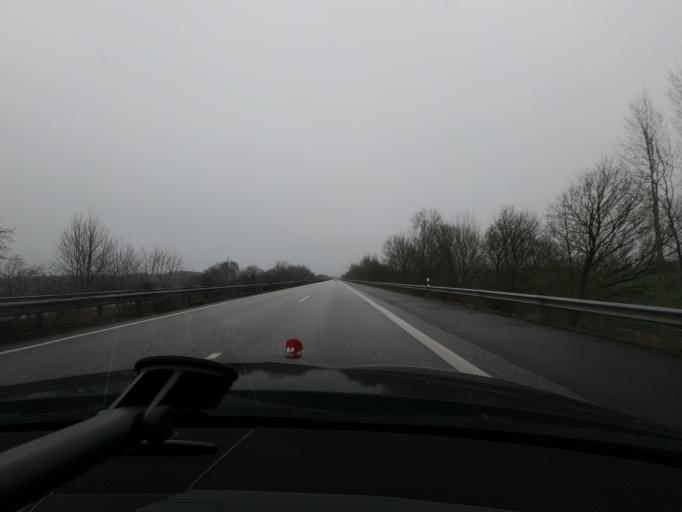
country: DE
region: Schleswig-Holstein
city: Bollingstedt
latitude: 54.6002
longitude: 9.4533
